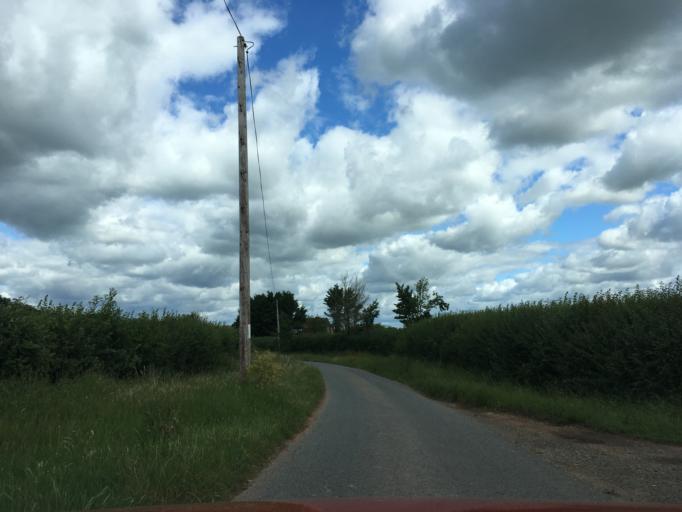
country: GB
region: England
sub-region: Gloucestershire
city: Newent
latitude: 51.8493
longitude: -2.3624
